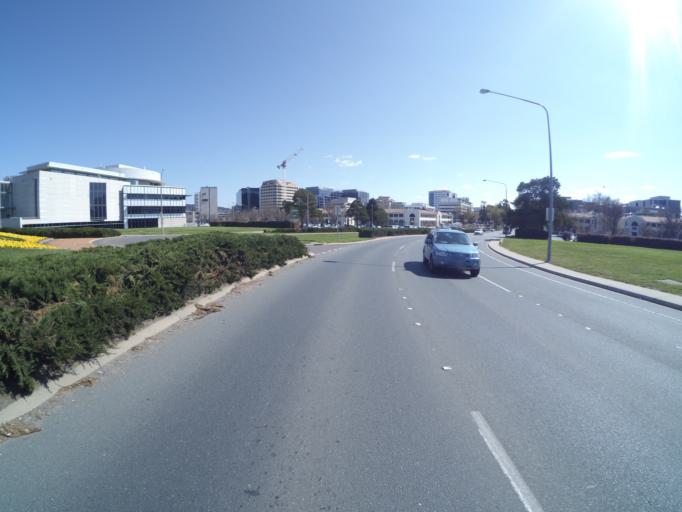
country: AU
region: Australian Capital Territory
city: Canberra
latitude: -35.2809
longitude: 149.1292
